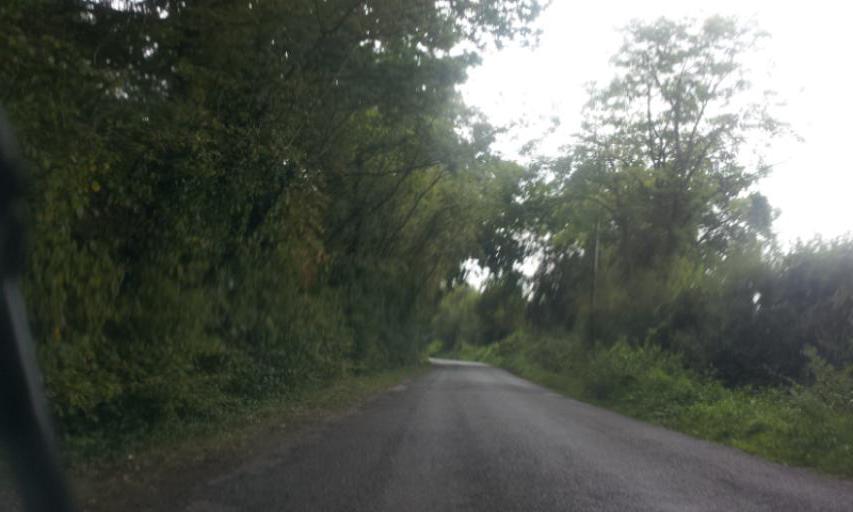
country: GB
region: England
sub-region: Kent
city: Yalding
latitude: 51.2032
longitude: 0.4171
